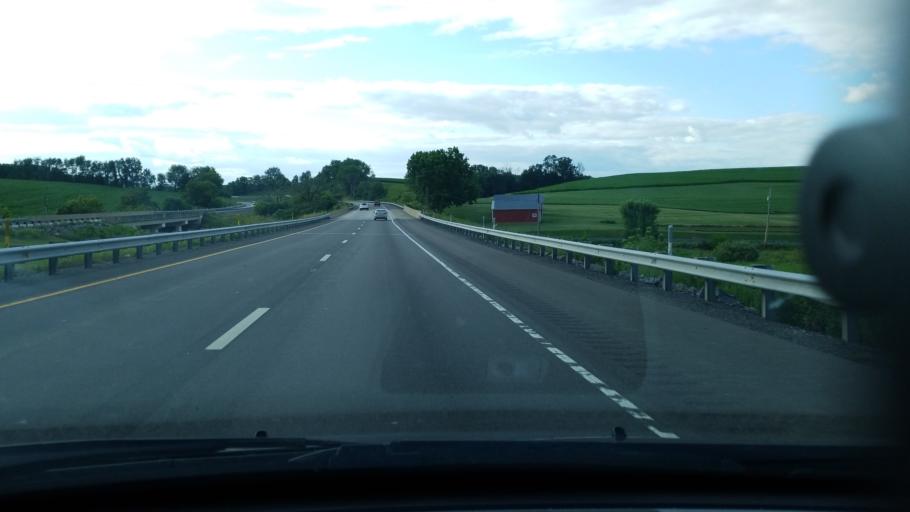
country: US
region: Pennsylvania
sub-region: Northumberland County
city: Milton
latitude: 41.0382
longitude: -76.8101
